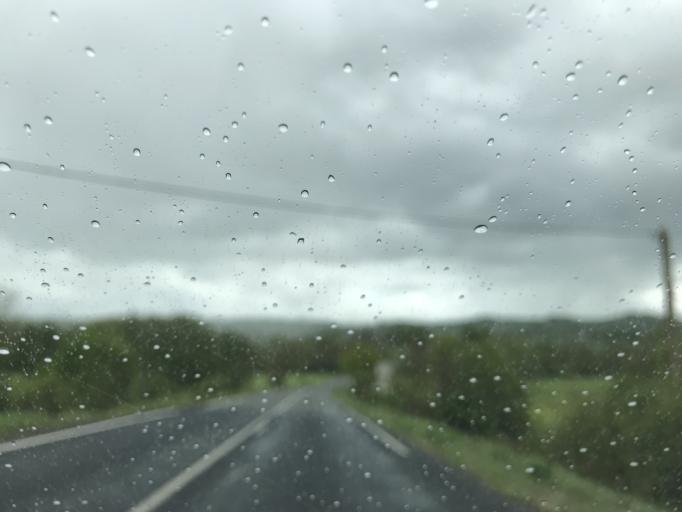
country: FR
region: Auvergne
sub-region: Departement du Puy-de-Dome
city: Billom
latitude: 45.7231
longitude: 3.3566
